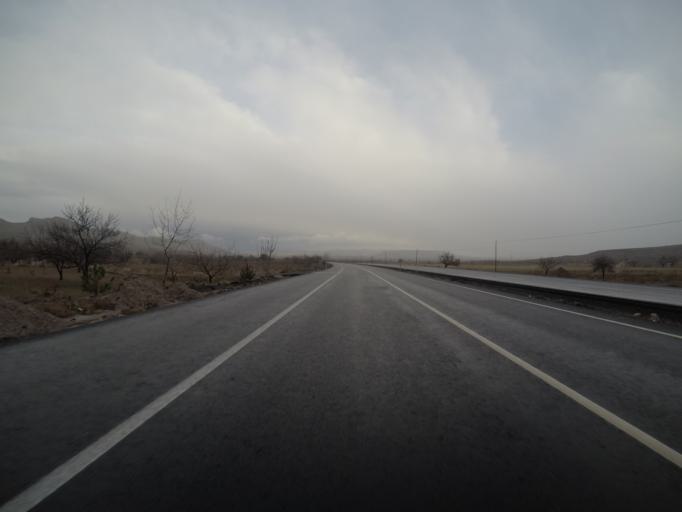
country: TR
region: Nevsehir
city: Goereme
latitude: 38.6769
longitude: 34.7696
